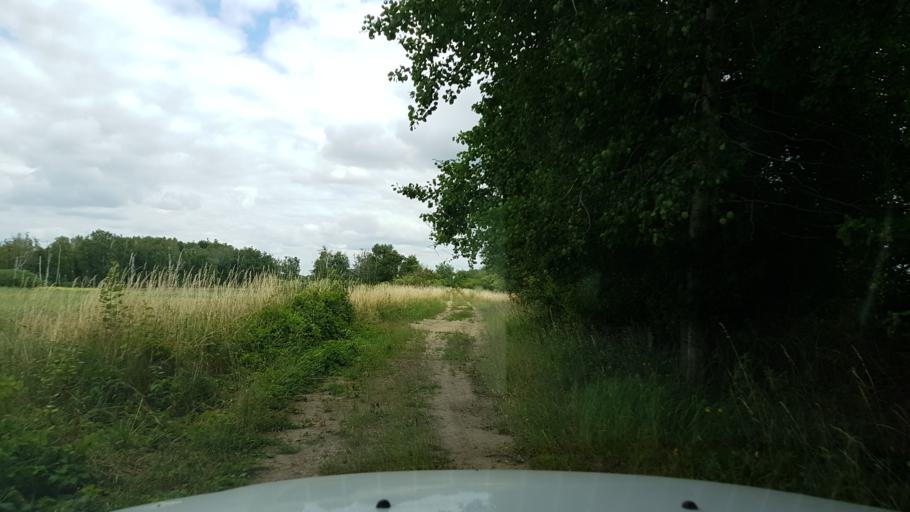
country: PL
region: West Pomeranian Voivodeship
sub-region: Powiat pyrzycki
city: Lipiany
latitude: 52.9449
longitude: 14.9344
